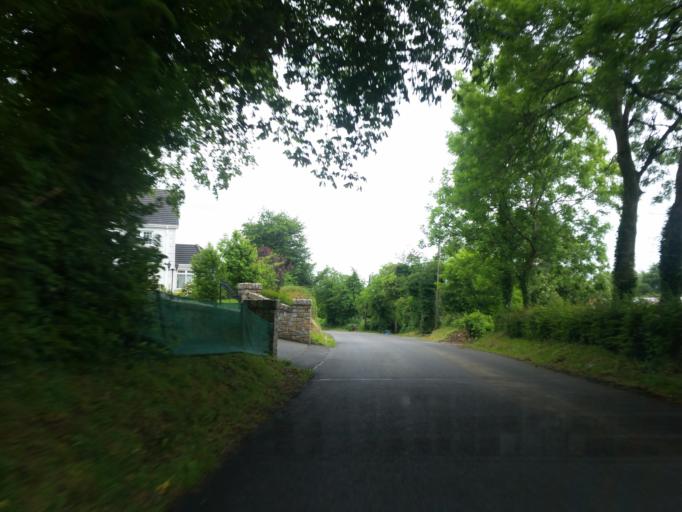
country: GB
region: Northern Ireland
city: Lisnaskea
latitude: 54.2328
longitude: -7.3622
